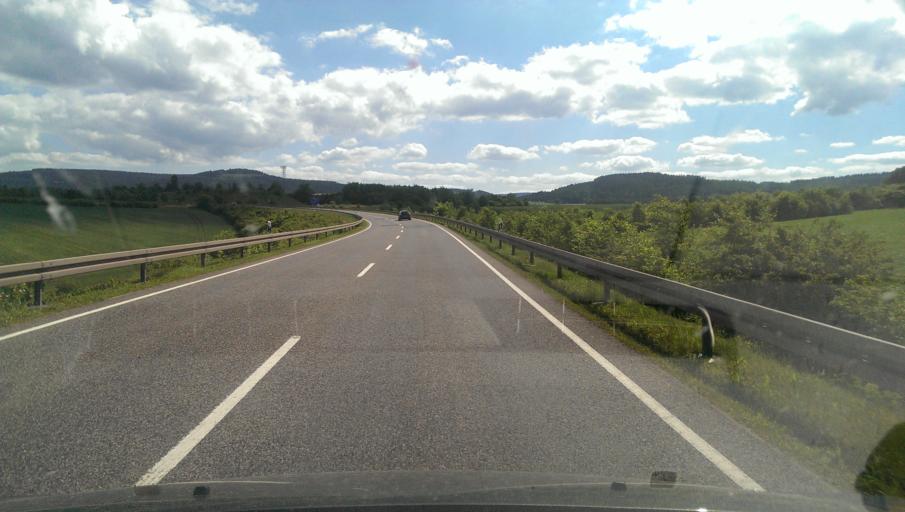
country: DE
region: Thuringia
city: Geschwenda
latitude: 50.7298
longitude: 10.8355
